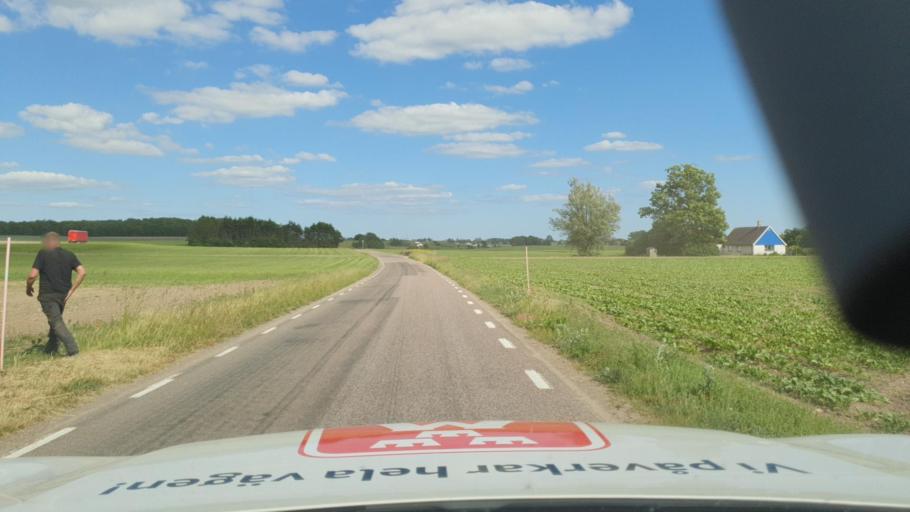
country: SE
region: Skane
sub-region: Ystads Kommun
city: Kopingebro
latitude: 55.4701
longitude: 13.9585
